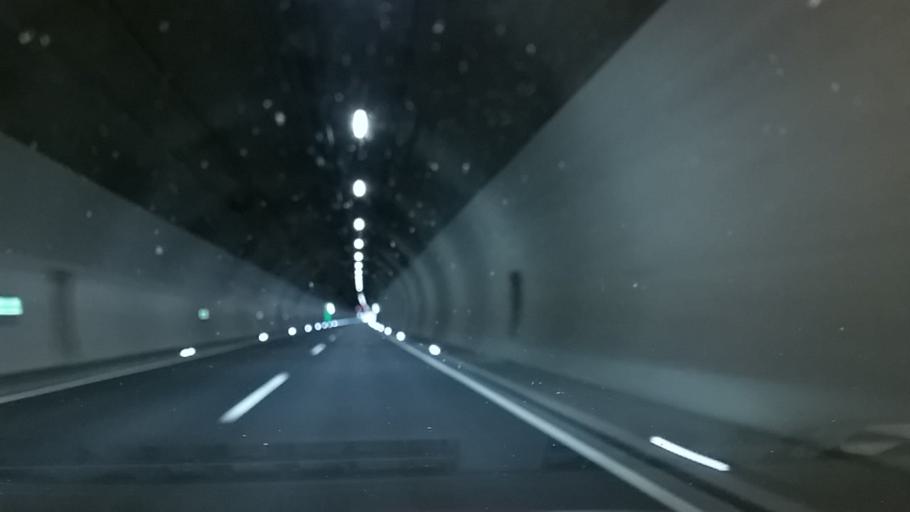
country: DE
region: Thuringia
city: Geschwenda
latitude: 50.7164
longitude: 10.8004
